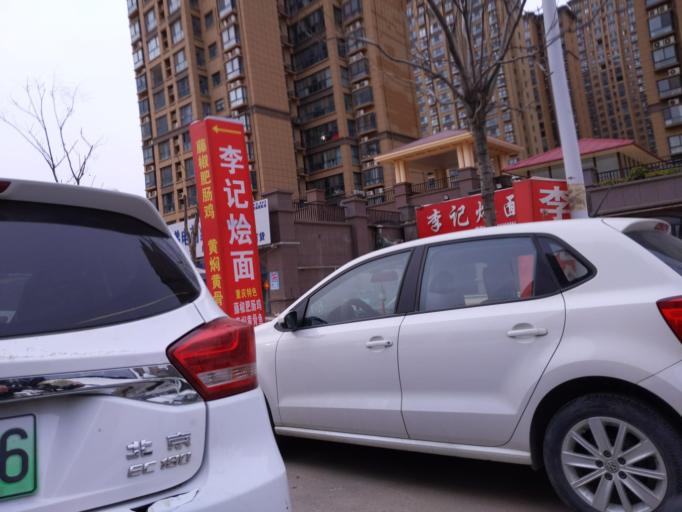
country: CN
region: Henan Sheng
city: Zhongyuanlu
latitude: 35.7430
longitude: 115.0713
